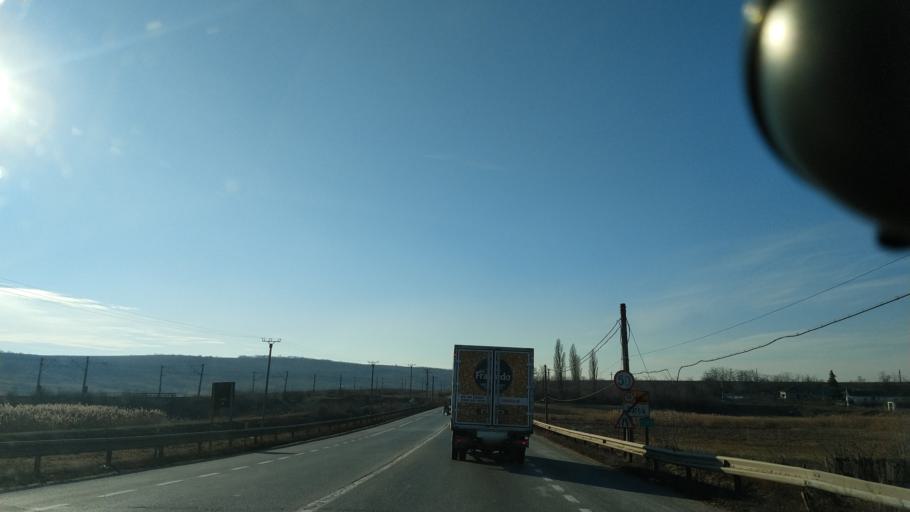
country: RO
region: Iasi
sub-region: Comuna Baltati
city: Baltati
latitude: 47.2247
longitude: 27.1801
